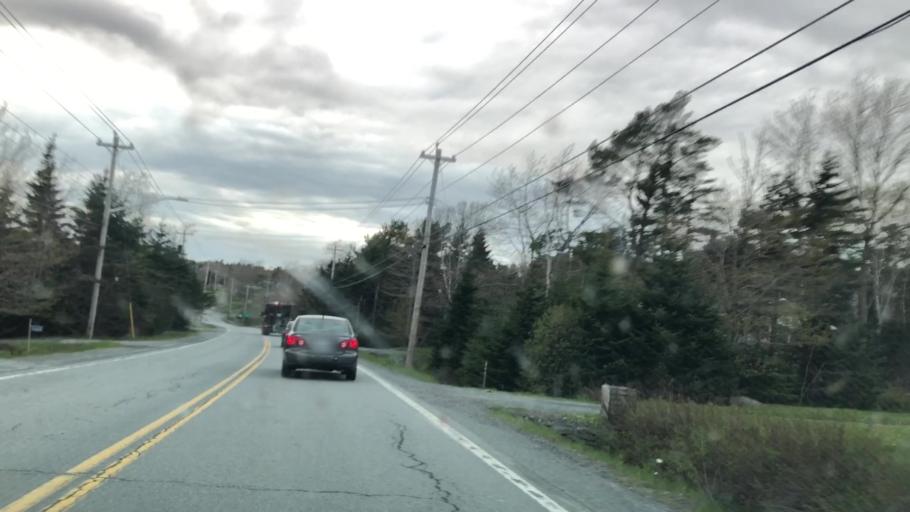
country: CA
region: Nova Scotia
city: Cole Harbour
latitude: 44.7839
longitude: -63.1615
